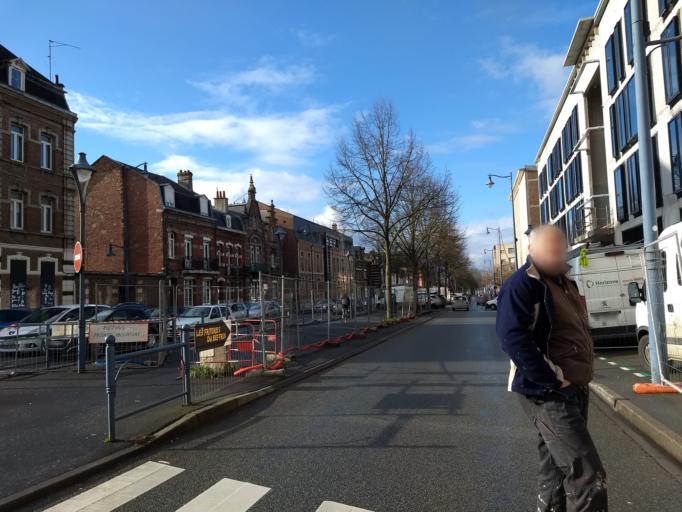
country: FR
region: Nord-Pas-de-Calais
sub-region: Departement du Pas-de-Calais
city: Arras
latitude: 50.2873
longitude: 2.7778
